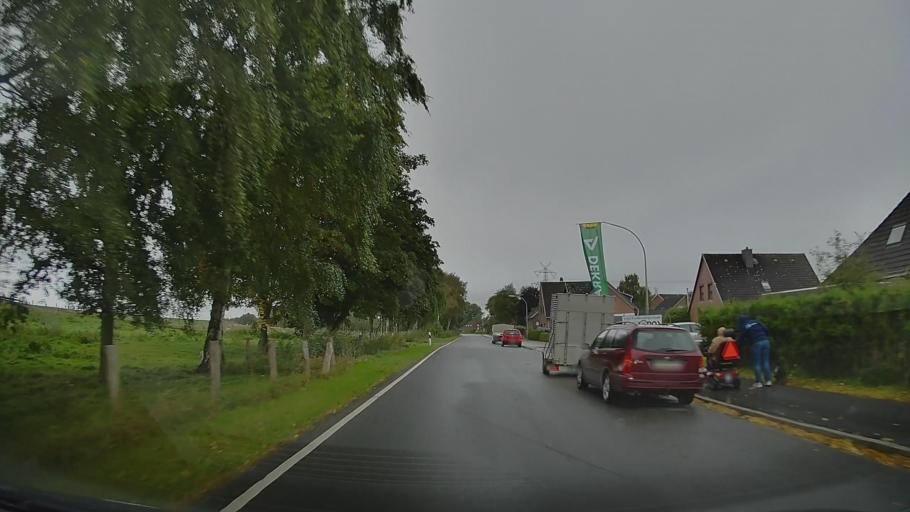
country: DE
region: Schleswig-Holstein
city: Sankt Margarethen
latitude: 53.8935
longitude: 9.2502
